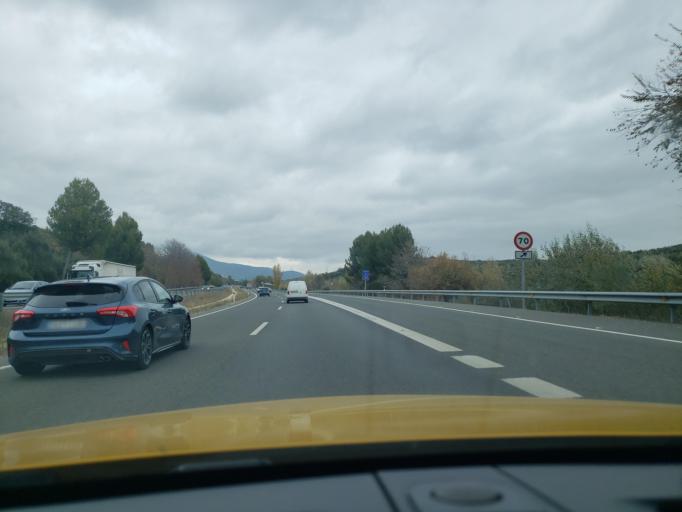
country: ES
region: Andalusia
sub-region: Provincia de Granada
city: Deifontes
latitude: 37.3401
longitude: -3.6217
